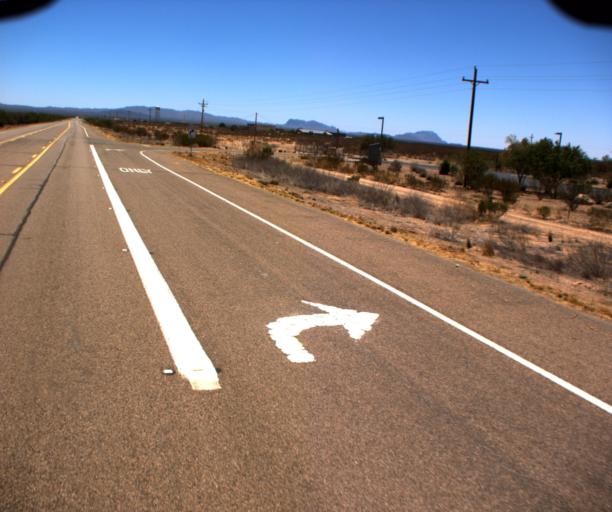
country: US
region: Arizona
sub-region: Pima County
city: Ajo
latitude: 32.1906
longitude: -112.4153
